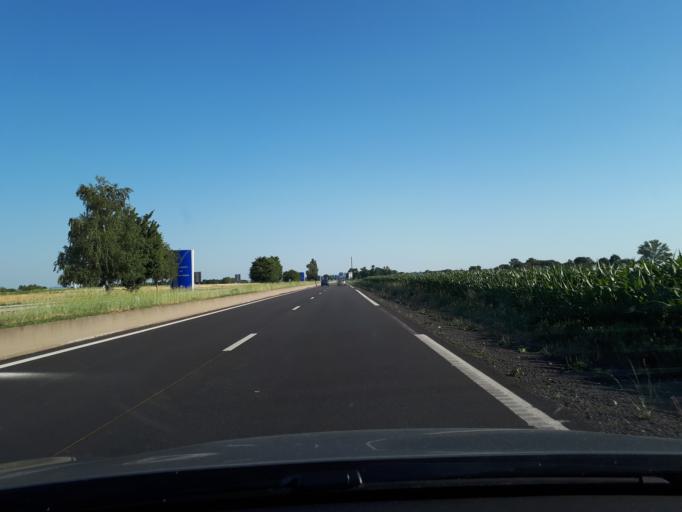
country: FR
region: Rhone-Alpes
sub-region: Departement du Rhone
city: Saint-Laurent-de-Mure
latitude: 45.7107
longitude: 5.0710
